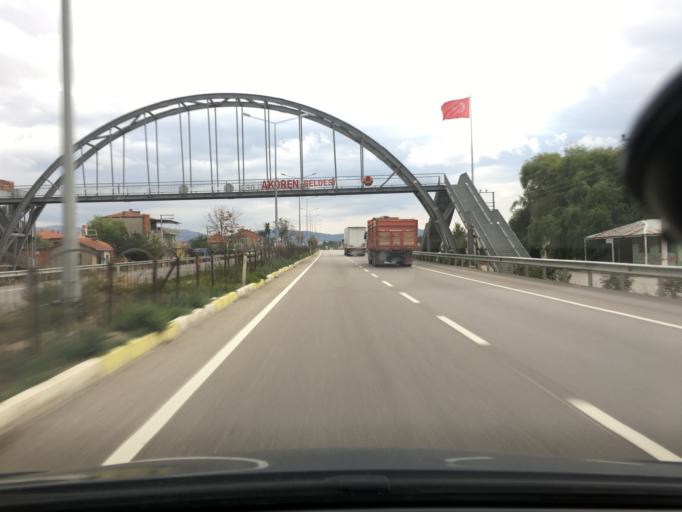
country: TR
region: Afyonkarahisar
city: Sincanli
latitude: 38.7757
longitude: 30.3717
